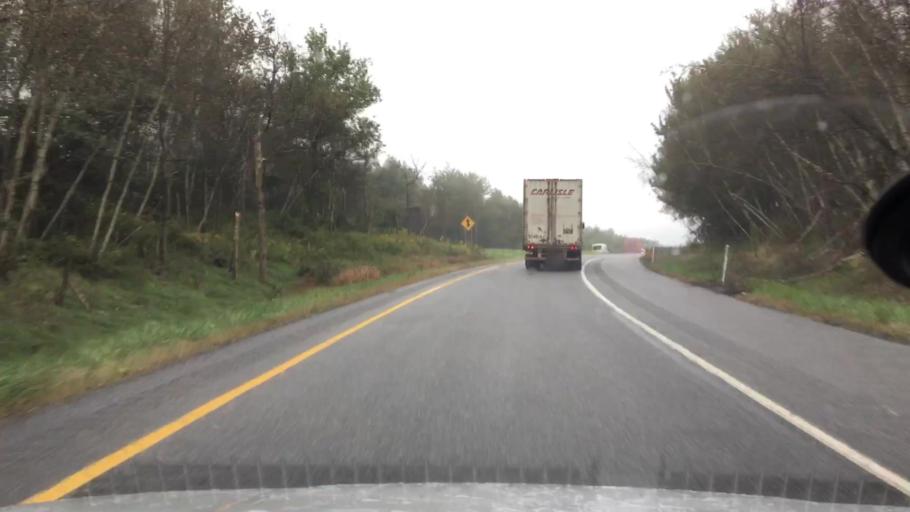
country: US
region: Pennsylvania
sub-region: Monroe County
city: Emerald Lakes
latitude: 41.0751
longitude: -75.3989
